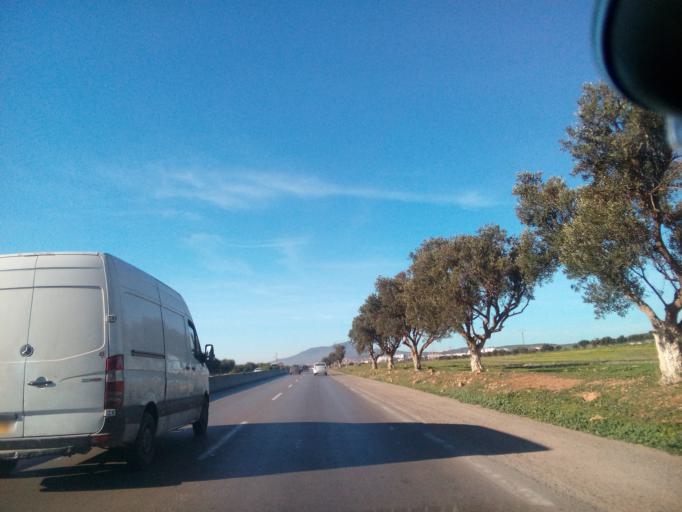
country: DZ
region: Oran
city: Ain el Bya
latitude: 35.7939
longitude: -0.3901
